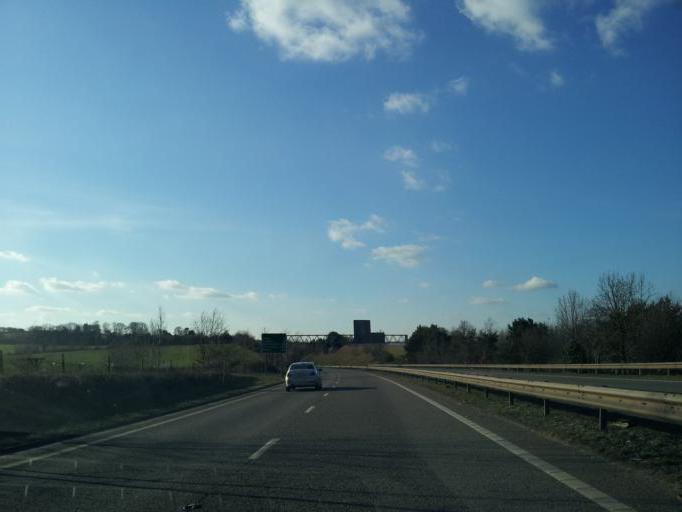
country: GB
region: England
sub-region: Devon
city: Exminster
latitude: 50.6847
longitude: -3.5224
